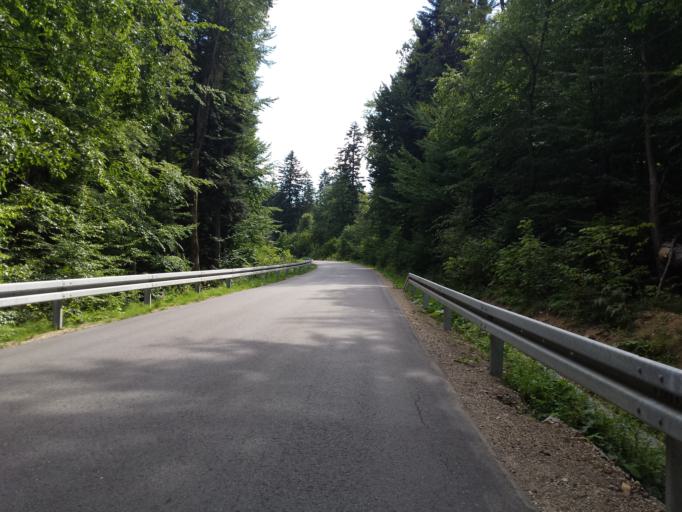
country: PL
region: Subcarpathian Voivodeship
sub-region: Powiat przemyski
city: Fredropol
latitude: 49.5957
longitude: 22.6419
